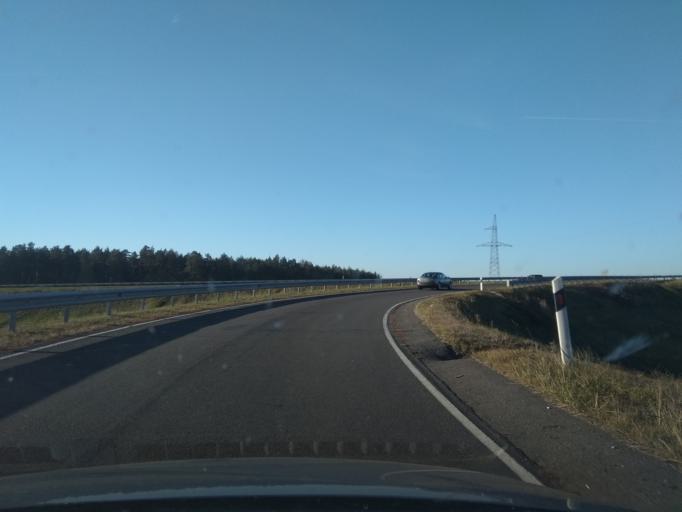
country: BY
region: Brest
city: Nyakhachava
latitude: 52.5741
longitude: 25.1097
